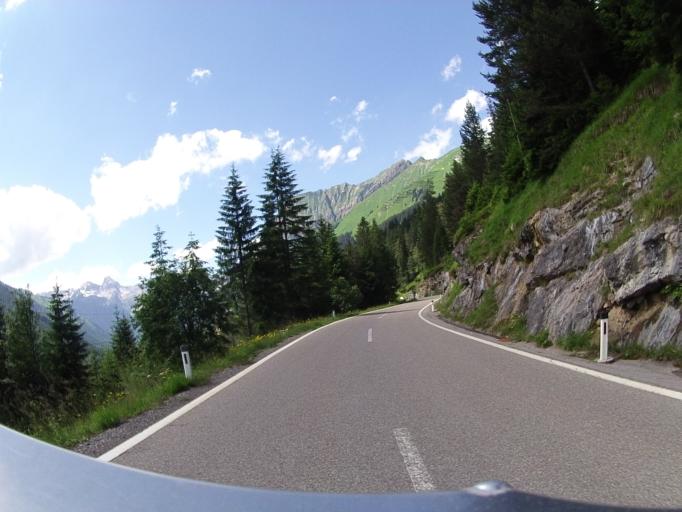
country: AT
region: Tyrol
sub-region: Politischer Bezirk Reutte
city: Elmen
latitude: 47.3020
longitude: 10.5976
